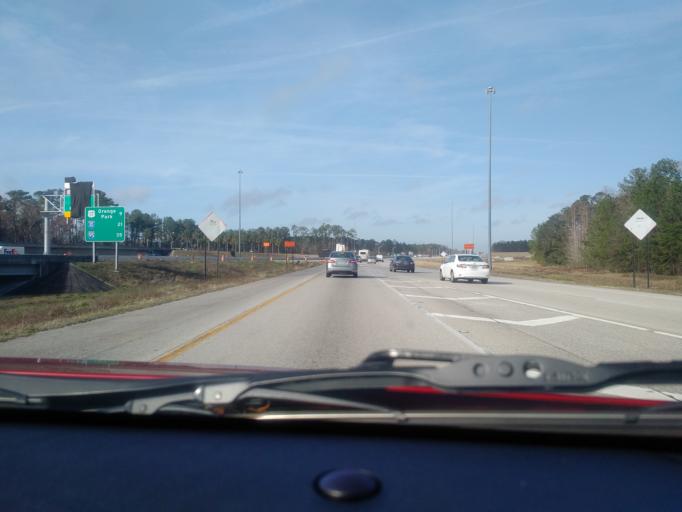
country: US
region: Florida
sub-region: Saint Johns County
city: Fruit Cove
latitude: 30.1675
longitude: -81.5624
